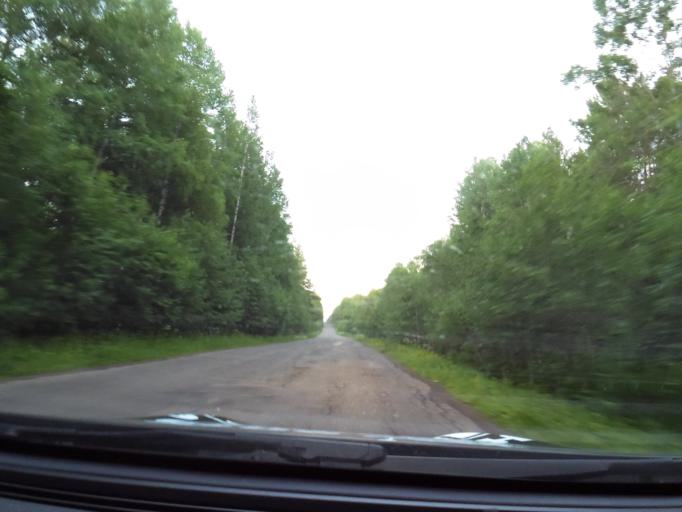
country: RU
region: Leningrad
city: Voznesen'ye
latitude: 60.8385
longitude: 35.6456
